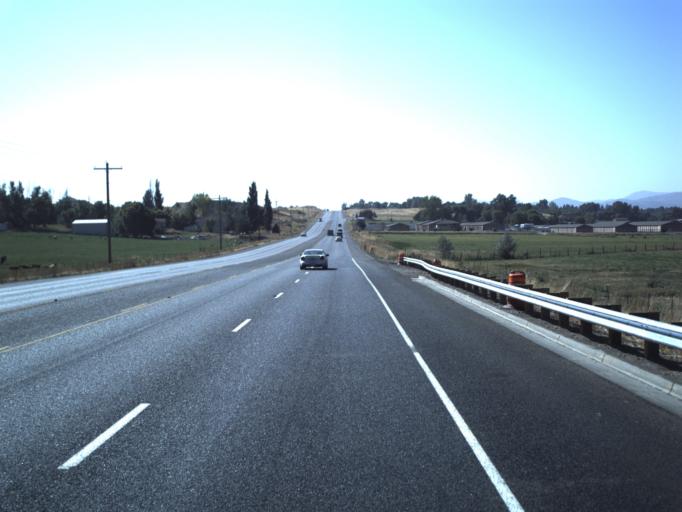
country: US
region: Utah
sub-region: Cache County
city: Nibley
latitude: 41.6554
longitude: -111.8329
